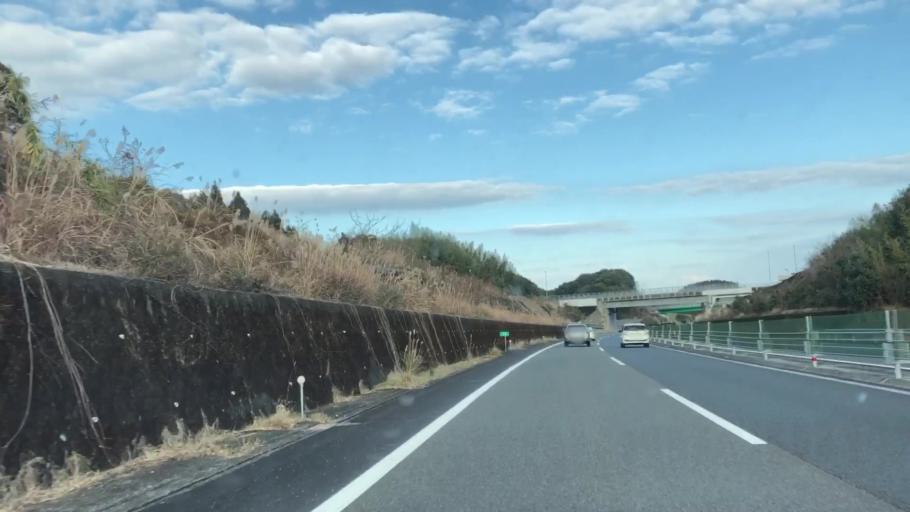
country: JP
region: Miyazaki
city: Miyazaki-shi
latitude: 31.8474
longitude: 131.3554
